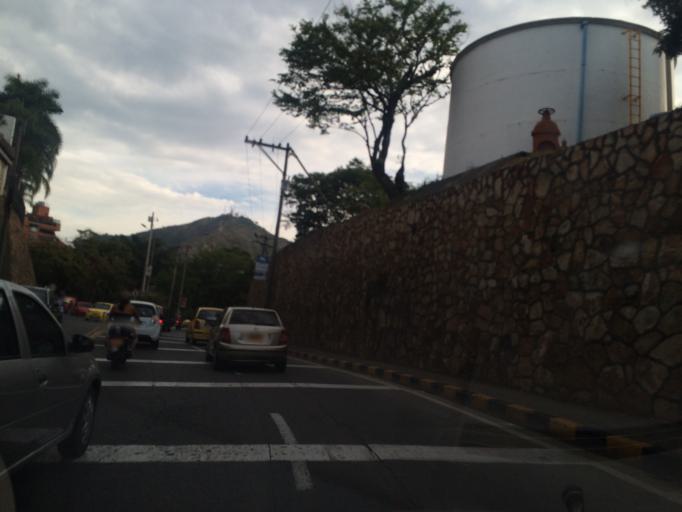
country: CO
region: Valle del Cauca
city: Cali
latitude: 3.4459
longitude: -76.5462
